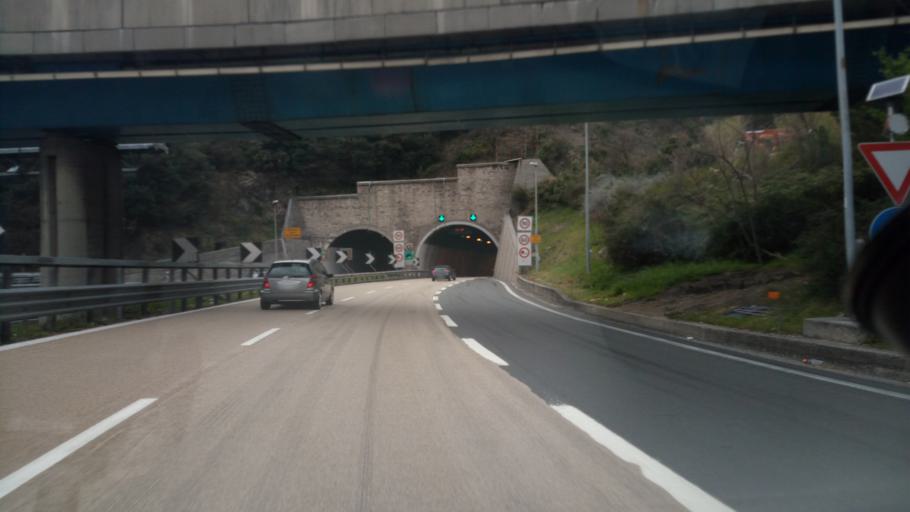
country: IT
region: Liguria
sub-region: Provincia di Genova
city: San Teodoro
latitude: 44.4241
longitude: 8.8687
